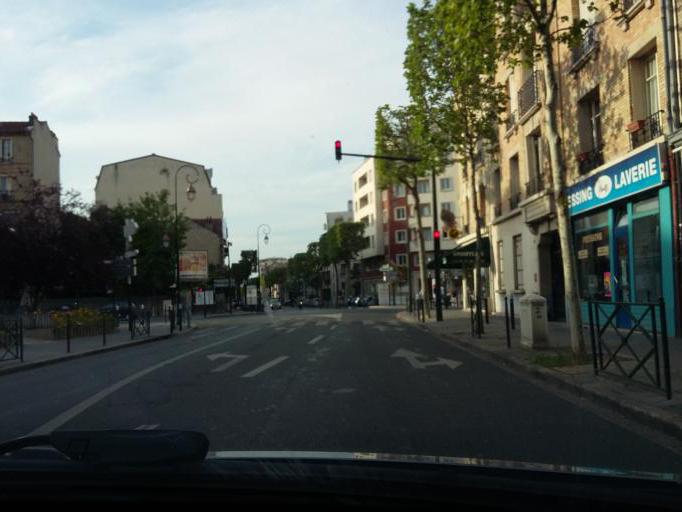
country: FR
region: Ile-de-France
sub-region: Departement des Hauts-de-Seine
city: Colombes
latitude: 48.9108
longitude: 2.2548
